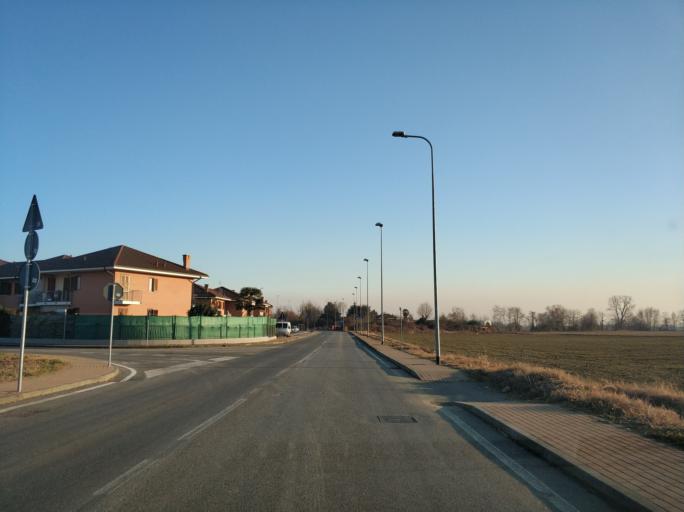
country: IT
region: Piedmont
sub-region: Provincia di Torino
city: San Maurizio
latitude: 45.2070
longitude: 7.6327
